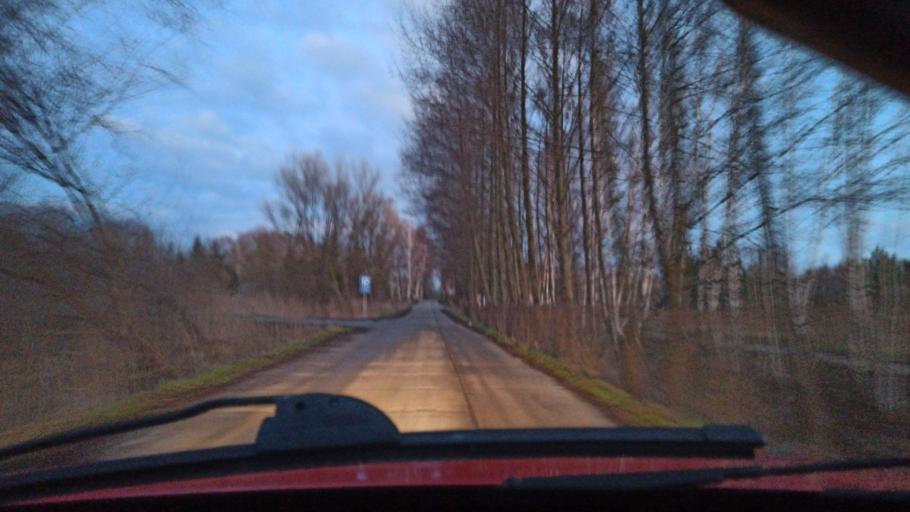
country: PL
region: Warmian-Masurian Voivodeship
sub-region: Powiat elblaski
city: Elblag
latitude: 54.1363
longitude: 19.4098
